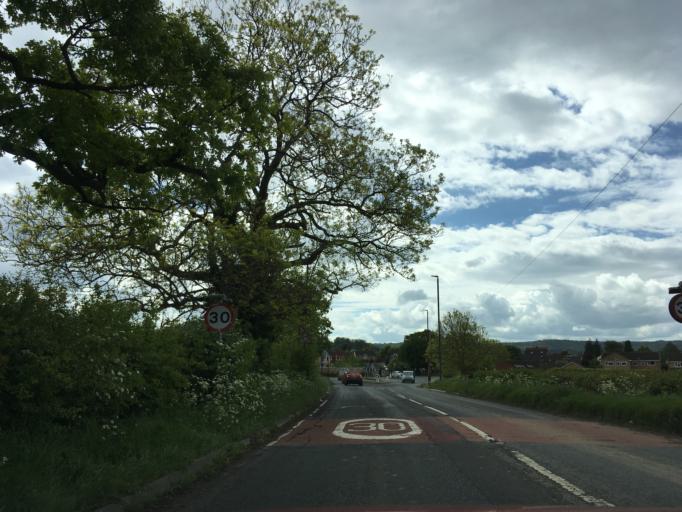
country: GB
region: England
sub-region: Gloucestershire
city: Stonehouse
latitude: 51.7574
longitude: -2.2830
